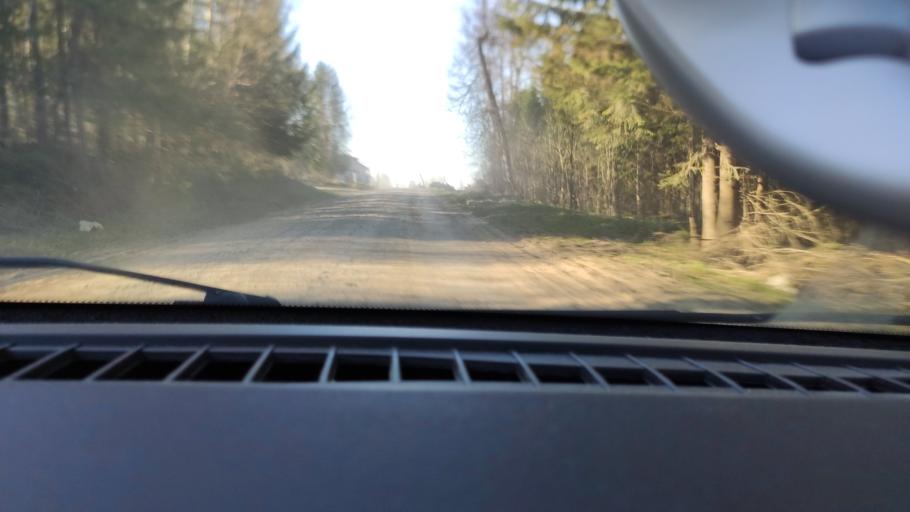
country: RU
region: Perm
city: Polazna
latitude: 58.1342
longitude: 56.4575
